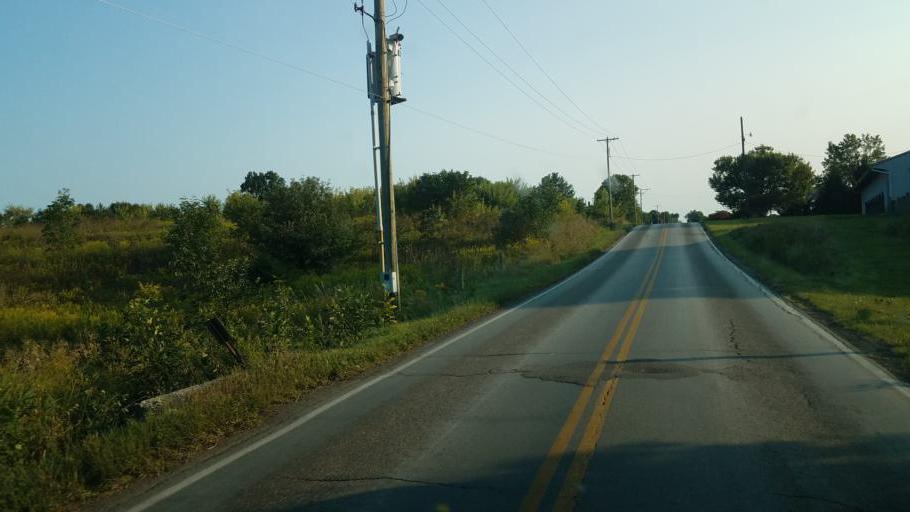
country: US
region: Ohio
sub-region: Wayne County
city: Apple Creek
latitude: 40.7795
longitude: -81.7885
